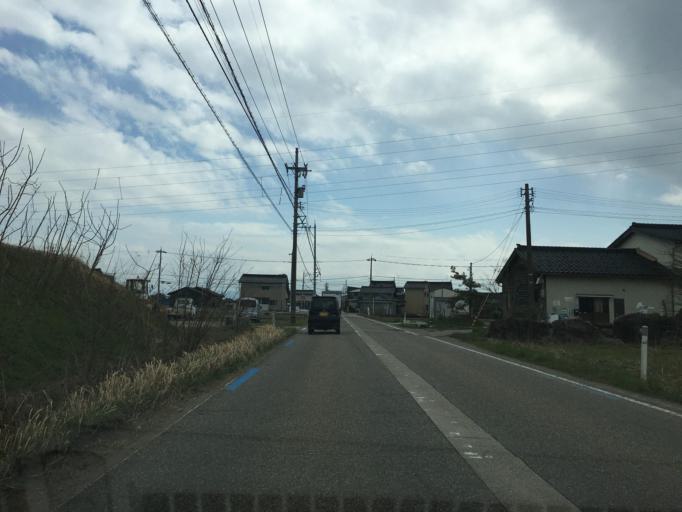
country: JP
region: Toyama
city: Kuragaki-kosugi
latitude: 36.6950
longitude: 137.1160
